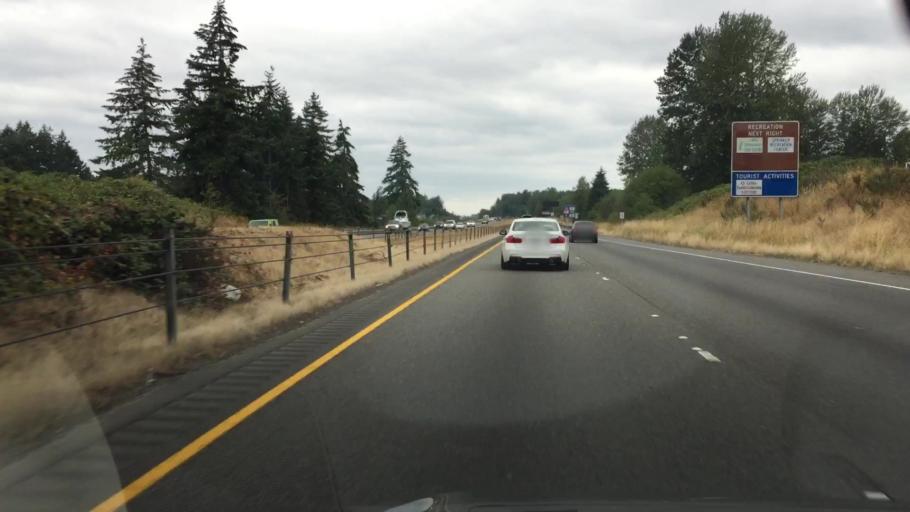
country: US
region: Washington
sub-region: Pierce County
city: Midland
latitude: 47.1590
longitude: -122.4070
